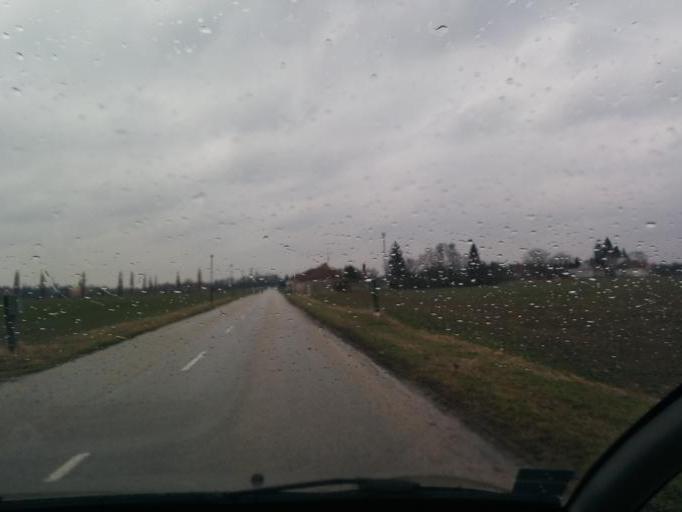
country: SK
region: Trnavsky
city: Sladkovicovo
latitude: 48.2144
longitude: 17.6352
